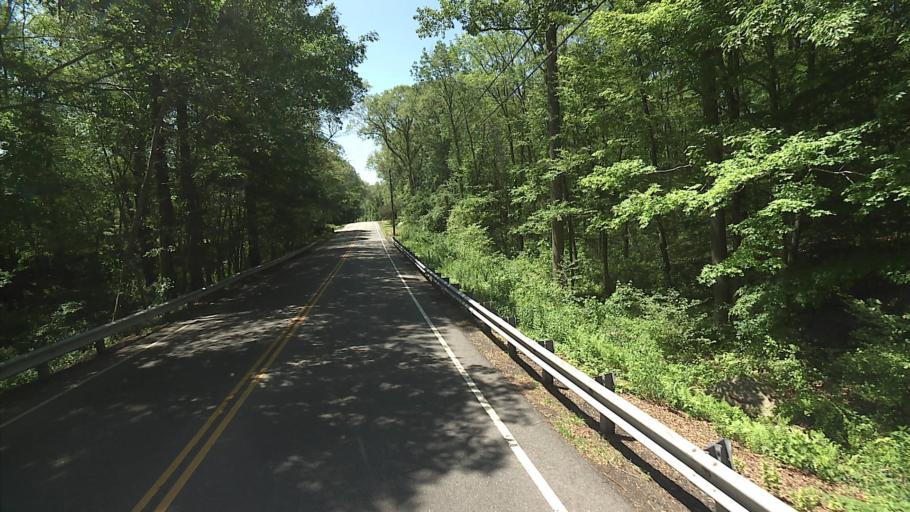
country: US
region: Rhode Island
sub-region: Washington County
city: Hopkinton
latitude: 41.4955
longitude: -71.8320
